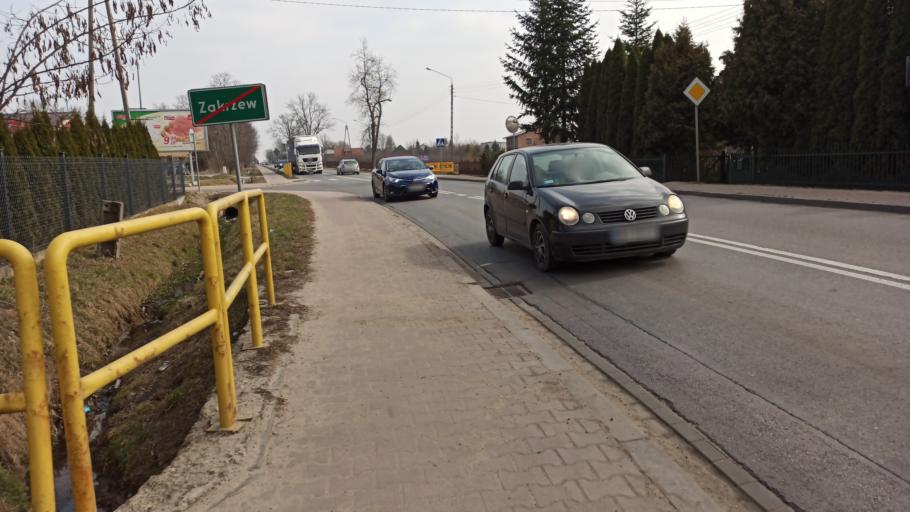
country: PL
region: Masovian Voivodeship
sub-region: Powiat radomski
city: Zakrzew
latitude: 51.4379
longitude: 21.0072
